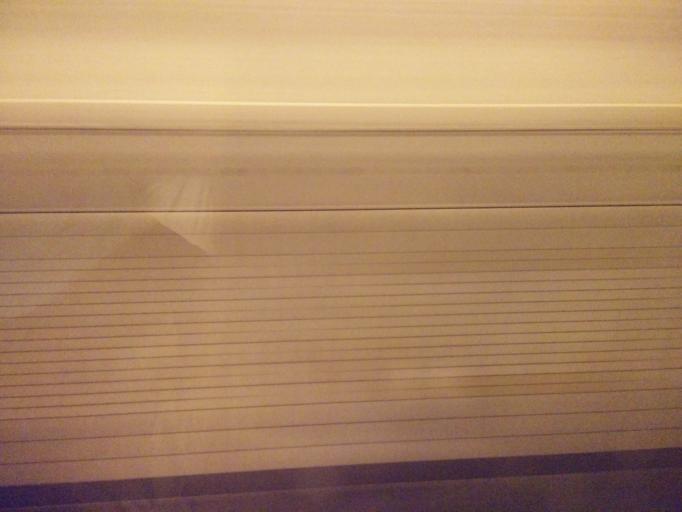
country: CA
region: British Columbia
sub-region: Fraser Valley Regional District
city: North Vancouver
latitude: 49.2832
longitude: -123.0320
